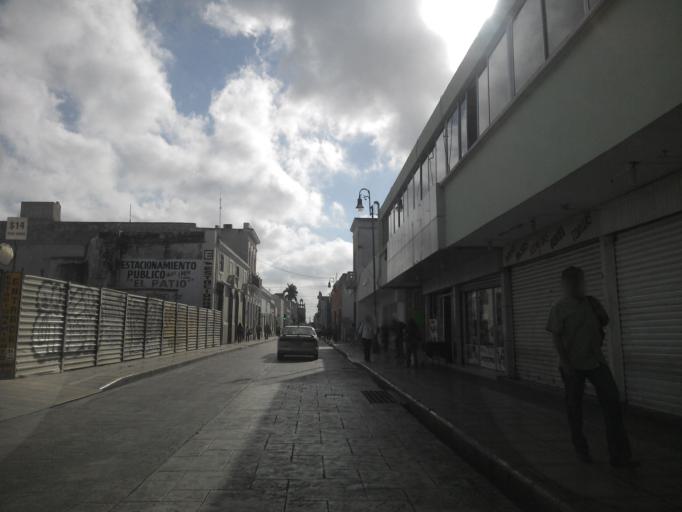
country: MX
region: Yucatan
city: Merida
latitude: 20.9682
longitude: -89.6198
